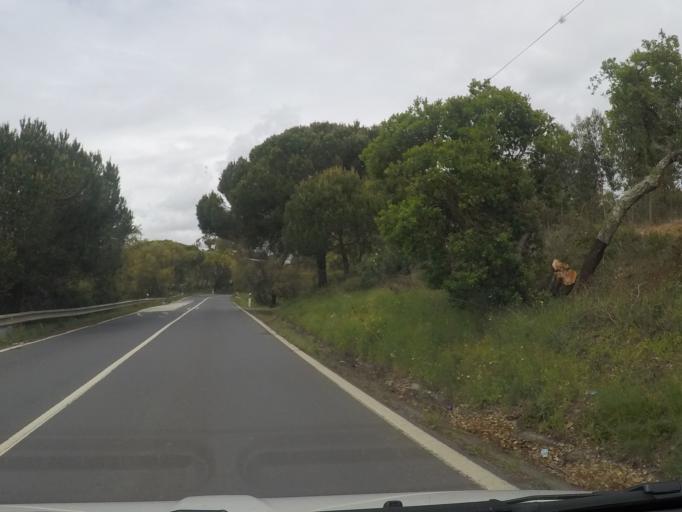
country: PT
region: Setubal
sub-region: Sines
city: Porto Covo
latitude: 37.8711
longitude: -8.7438
